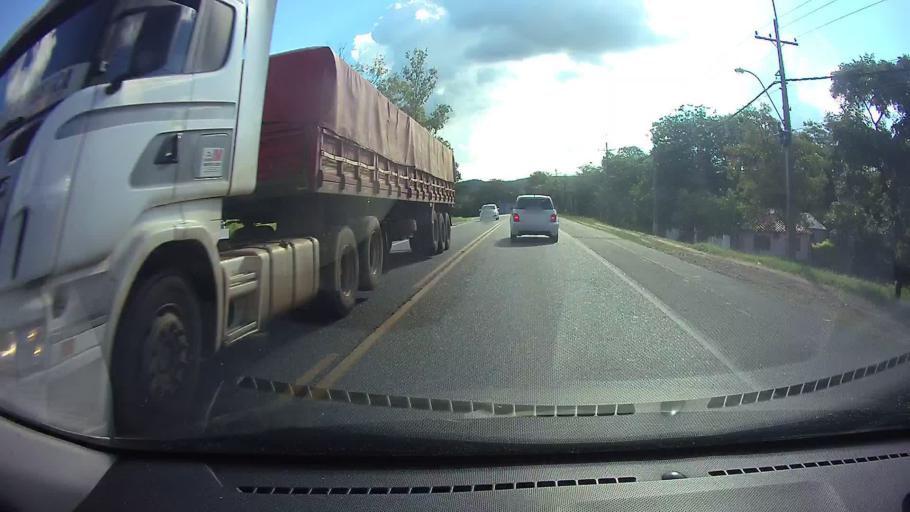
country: PY
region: Cordillera
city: Caacupe
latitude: -25.3854
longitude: -57.0557
